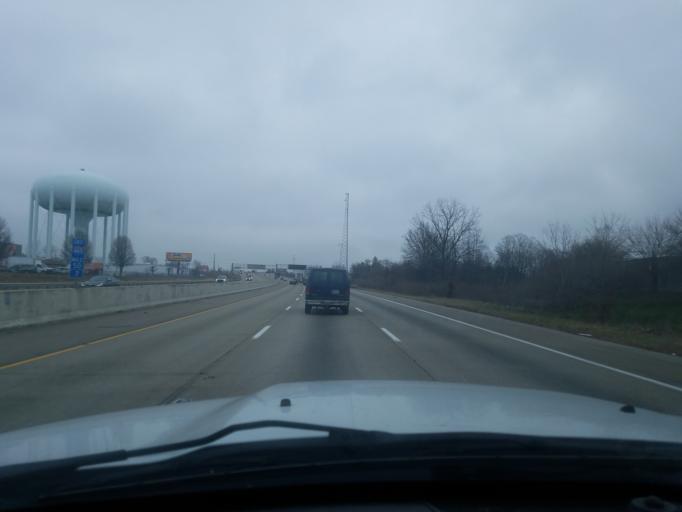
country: US
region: Indiana
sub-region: Marion County
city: Beech Grove
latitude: 39.7074
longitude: -86.0625
